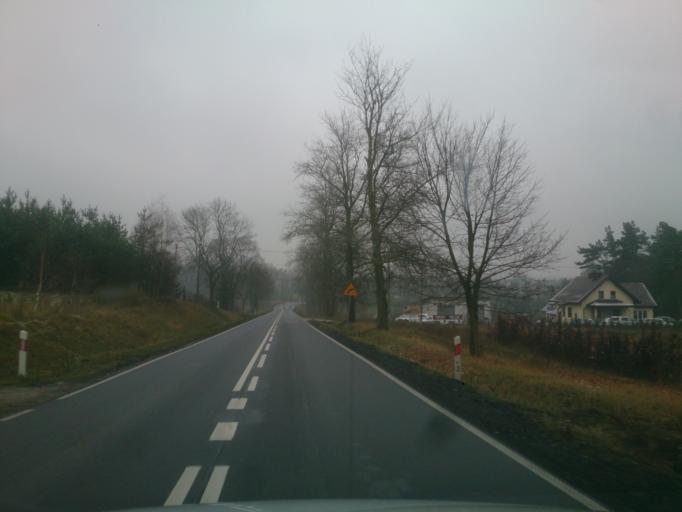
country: PL
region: Kujawsko-Pomorskie
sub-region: Powiat rypinski
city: Rypin
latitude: 53.0885
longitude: 19.4133
